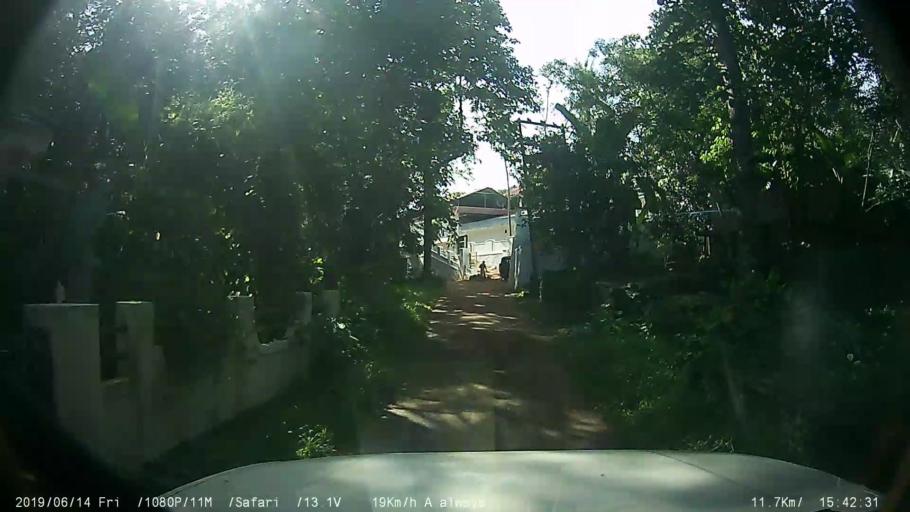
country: IN
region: Kerala
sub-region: Kottayam
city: Palackattumala
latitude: 9.7774
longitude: 76.6101
